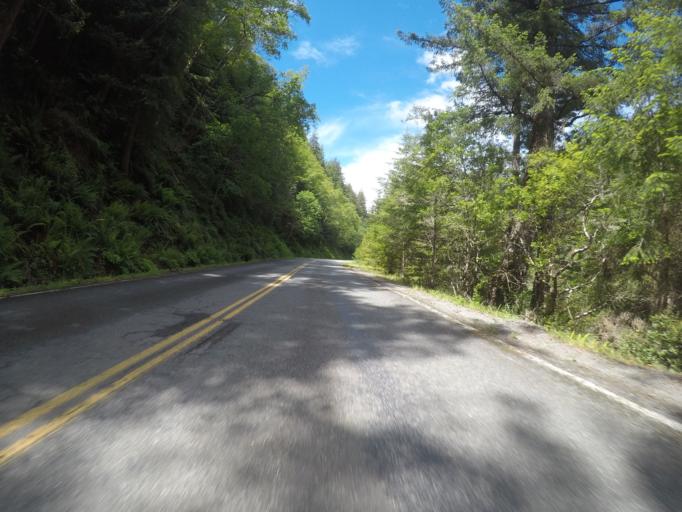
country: US
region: California
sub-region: Del Norte County
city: Bertsch-Oceanview
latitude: 41.7949
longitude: -124.0368
